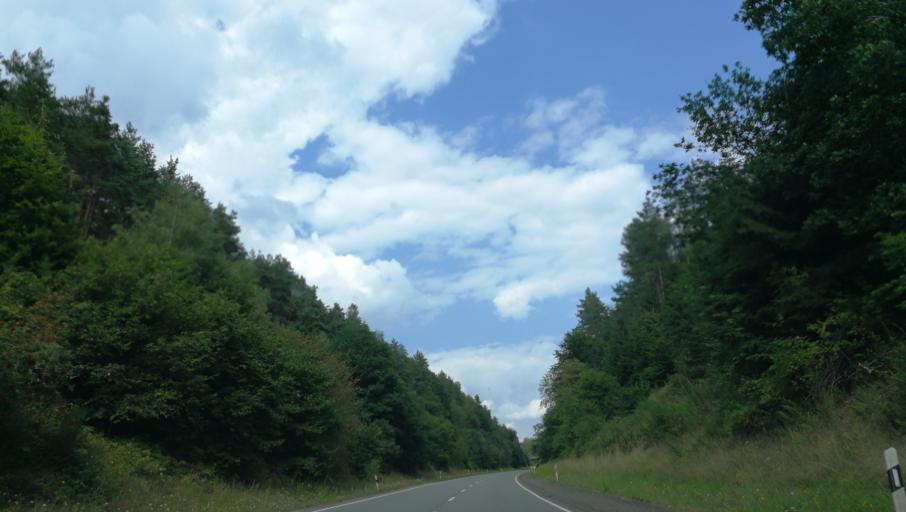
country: DE
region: Saarland
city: Losheim
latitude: 49.5068
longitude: 6.7120
